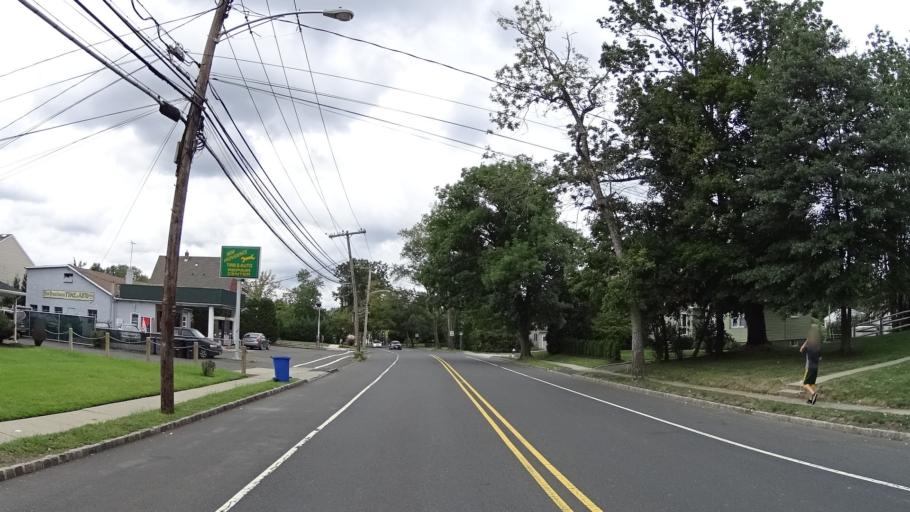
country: US
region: New Jersey
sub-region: Union County
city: New Providence
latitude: 40.7074
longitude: -74.4015
